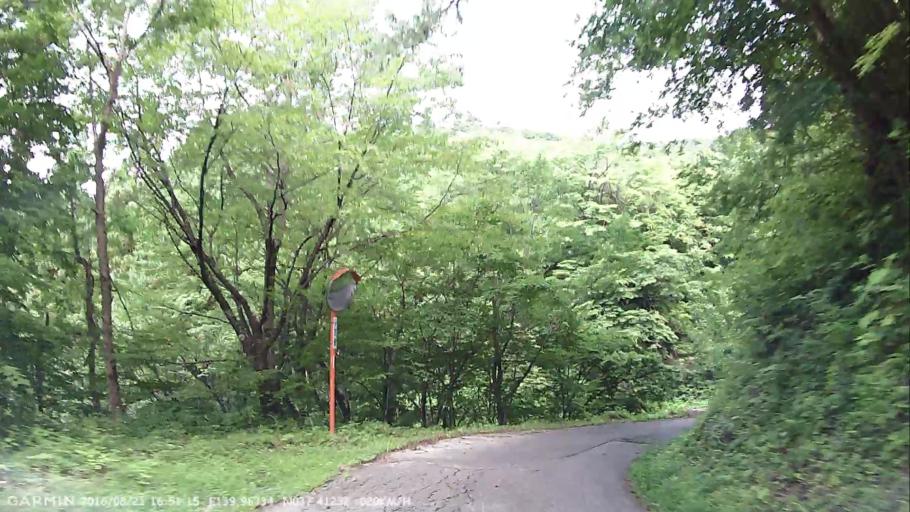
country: JP
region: Fukushima
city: Inawashiro
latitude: 37.4123
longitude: 139.9633
